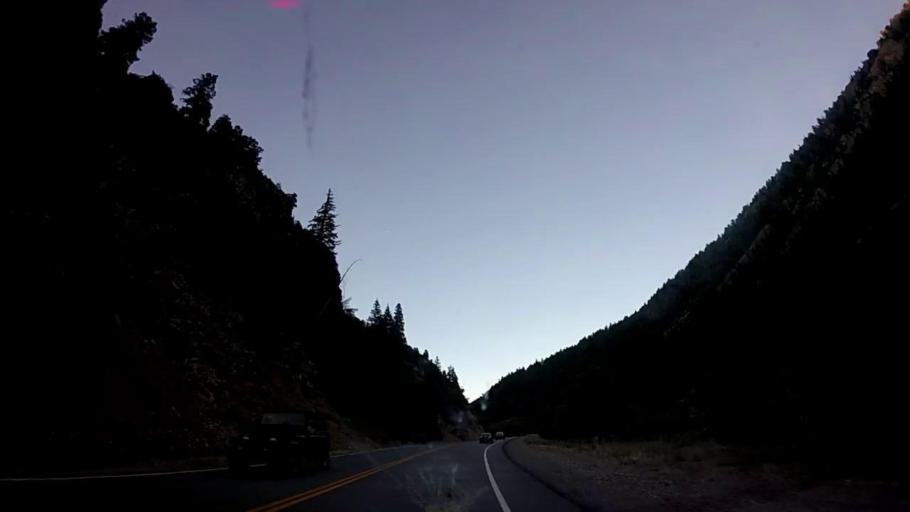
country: US
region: Utah
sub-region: Salt Lake County
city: Mount Olympus
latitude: 40.6398
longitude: -111.6925
